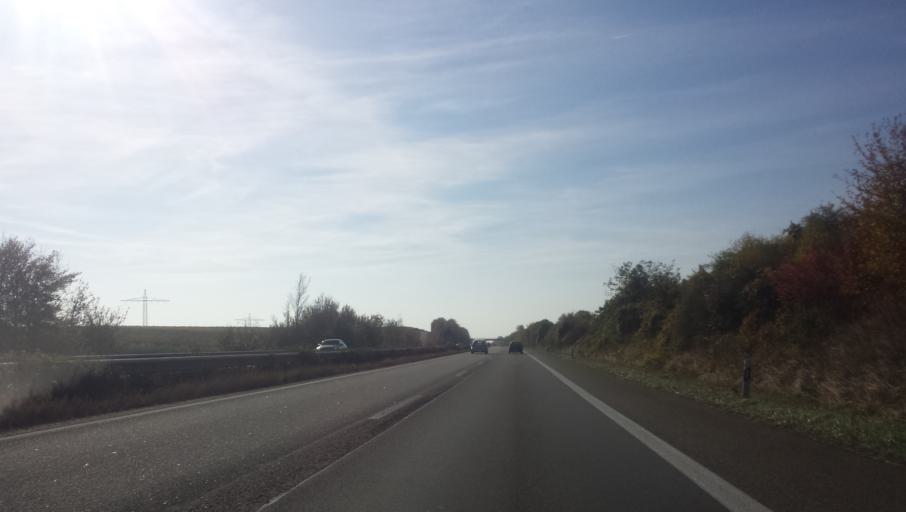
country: DE
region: Rheinland-Pfalz
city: Knoringen
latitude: 49.2462
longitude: 8.1490
